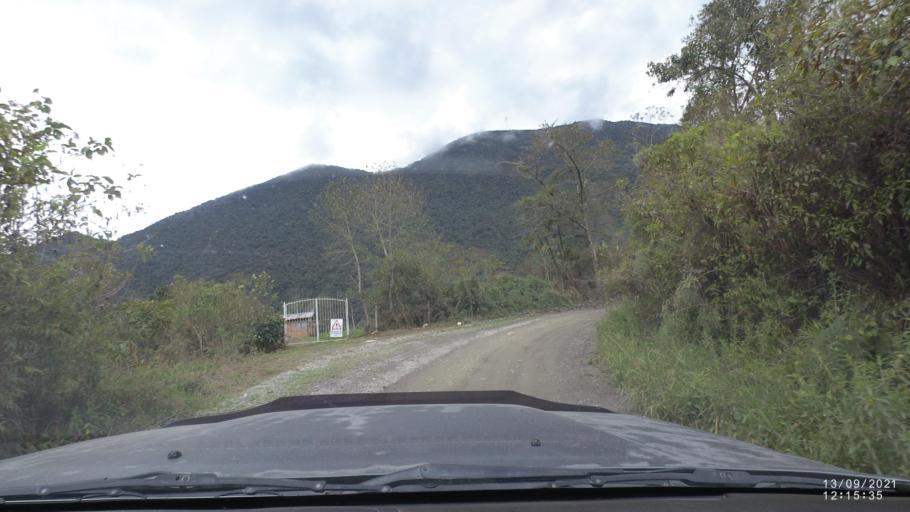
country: BO
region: Cochabamba
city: Colomi
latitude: -17.2227
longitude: -65.8221
